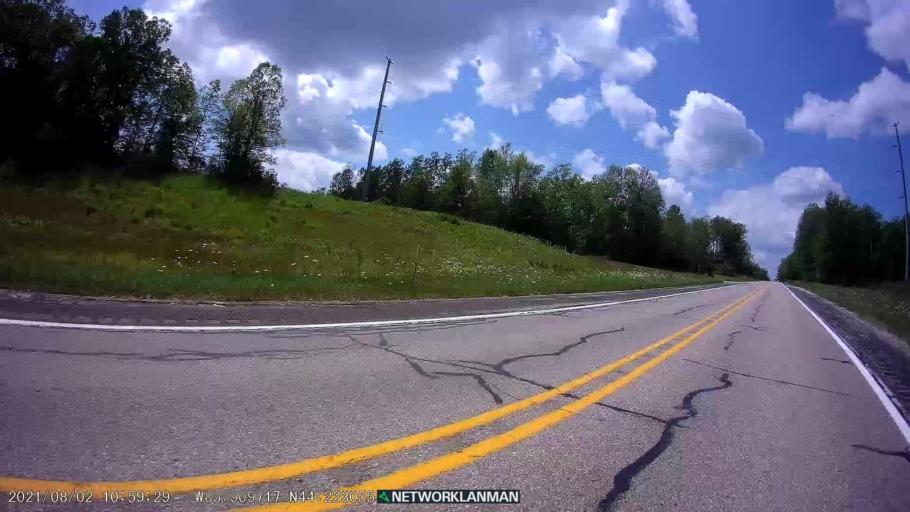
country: US
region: Michigan
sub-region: Lake County
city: Baldwin
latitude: 44.2231
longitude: -85.9101
